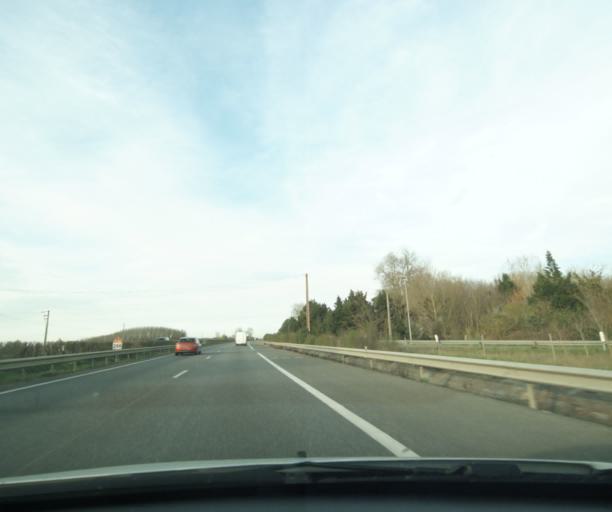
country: FR
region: Midi-Pyrenees
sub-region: Departement de la Haute-Garonne
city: Le Fauga
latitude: 43.4087
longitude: 1.2942
